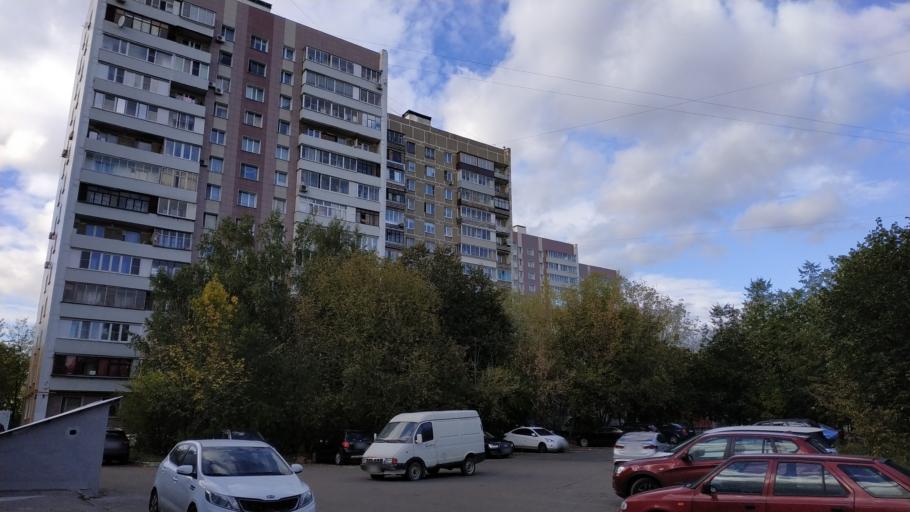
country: RU
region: Moscow
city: Metrogorodok
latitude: 55.7956
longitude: 37.7690
